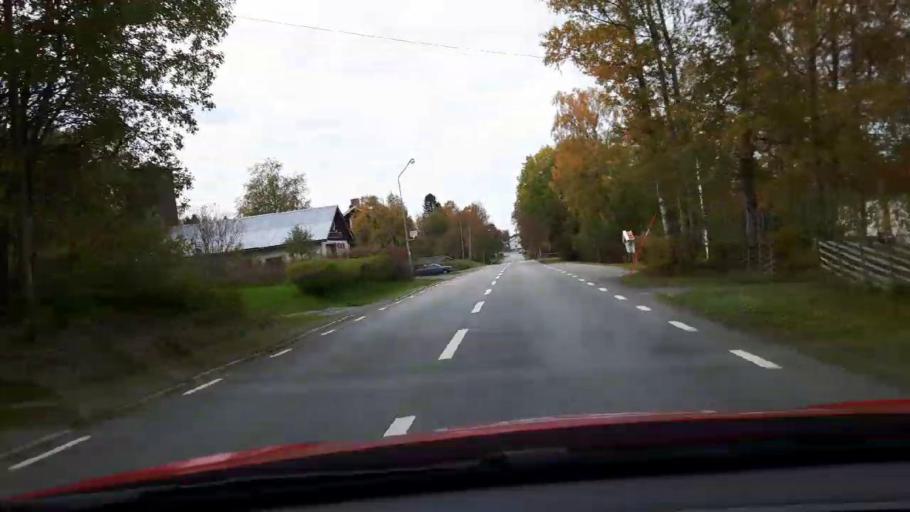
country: SE
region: Jaemtland
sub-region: Krokoms Kommun
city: Krokom
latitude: 63.1716
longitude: 14.1031
